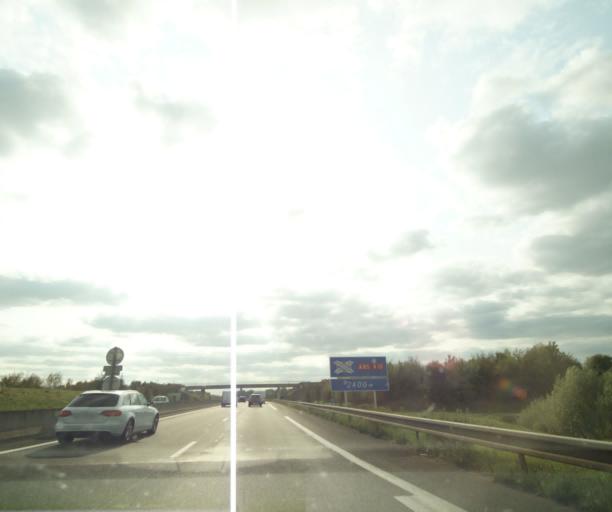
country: FR
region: Centre
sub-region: Departement d'Indre-et-Loire
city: Veigne
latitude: 47.3122
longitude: 0.7339
